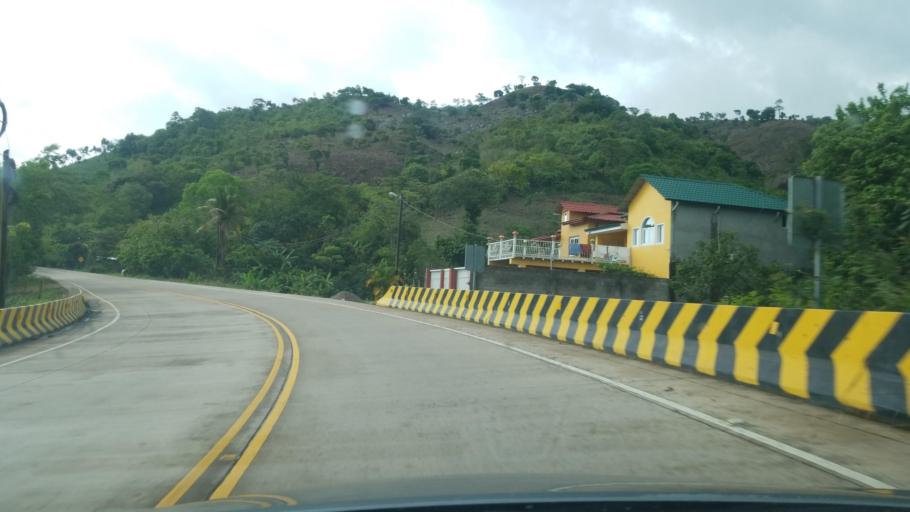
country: HN
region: Copan
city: Copan
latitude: 14.8451
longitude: -89.1891
